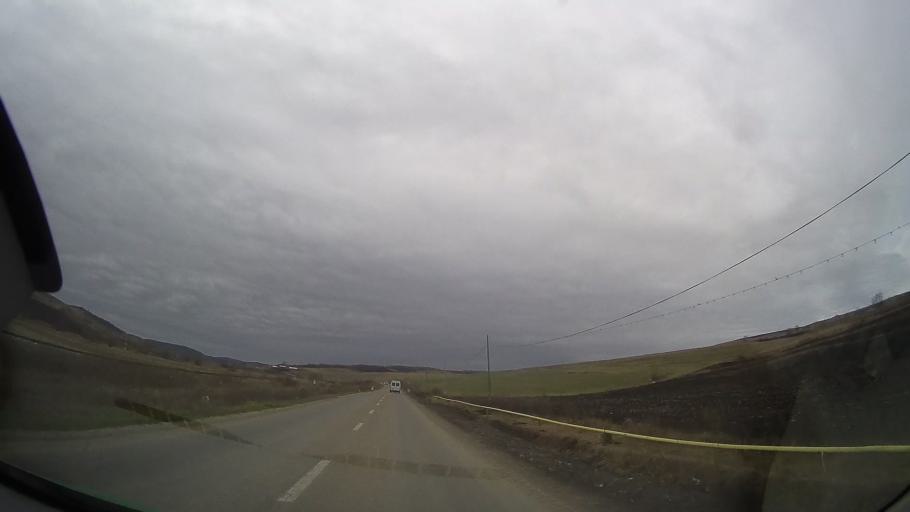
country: RO
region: Cluj
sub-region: Comuna Catina
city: Catina
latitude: 46.8091
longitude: 24.2197
